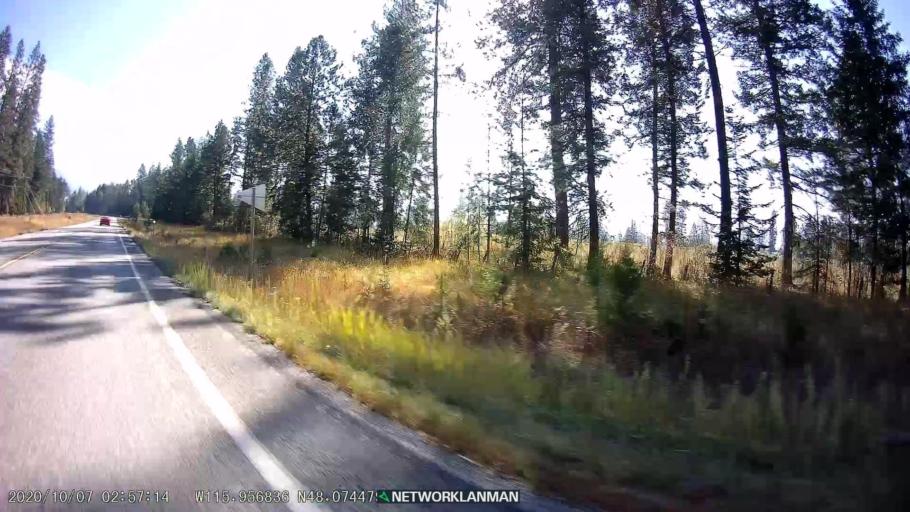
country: US
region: Montana
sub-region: Lincoln County
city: Libby
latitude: 48.0743
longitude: -115.9564
